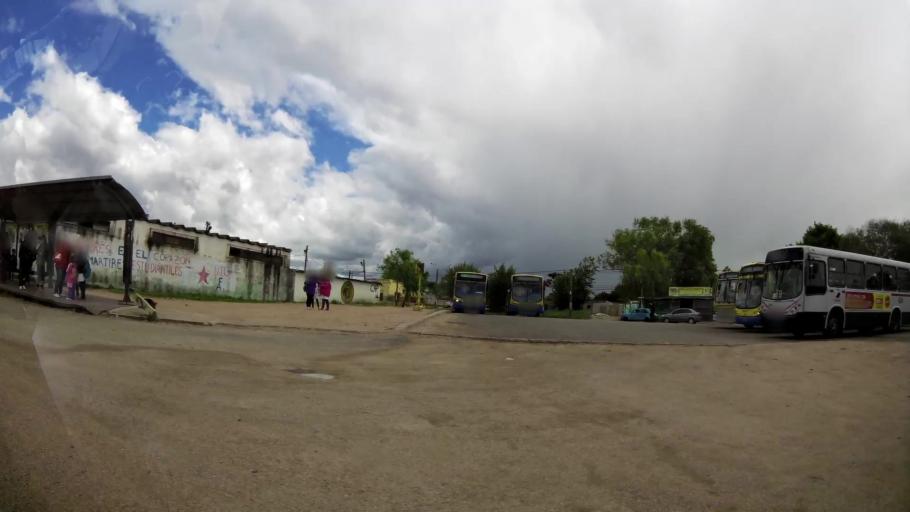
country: UY
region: Canelones
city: La Paz
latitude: -34.8065
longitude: -56.1622
